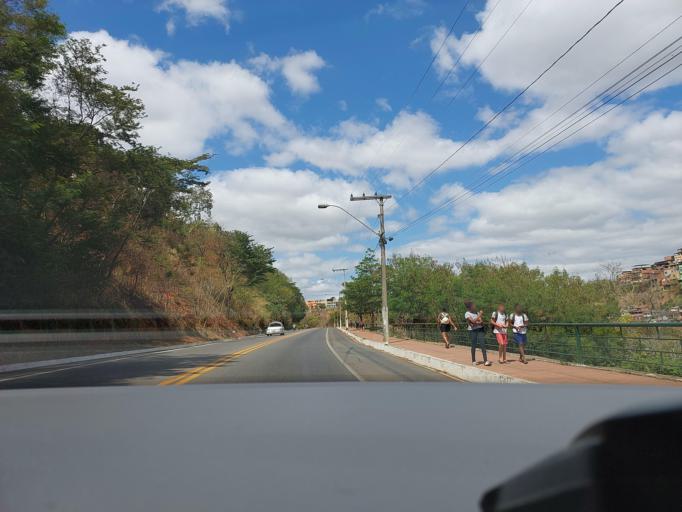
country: BR
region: Minas Gerais
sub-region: Muriae
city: Muriae
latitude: -21.1268
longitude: -42.3508
